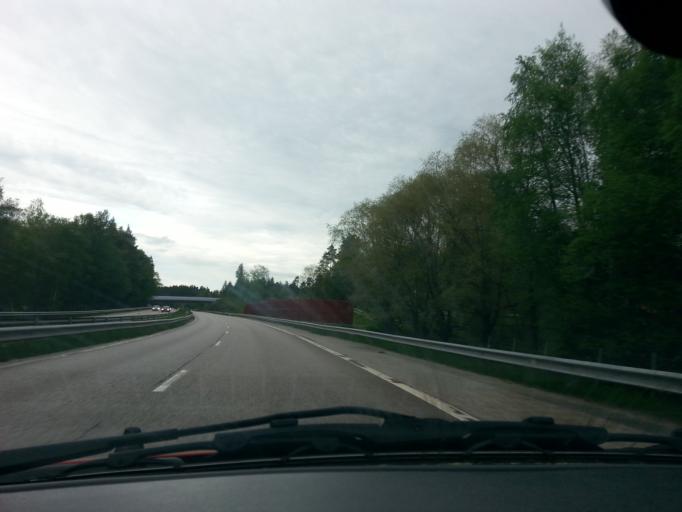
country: SE
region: Vaestra Goetaland
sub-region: Alingsas Kommun
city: Ingared
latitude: 57.8731
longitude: 12.4929
